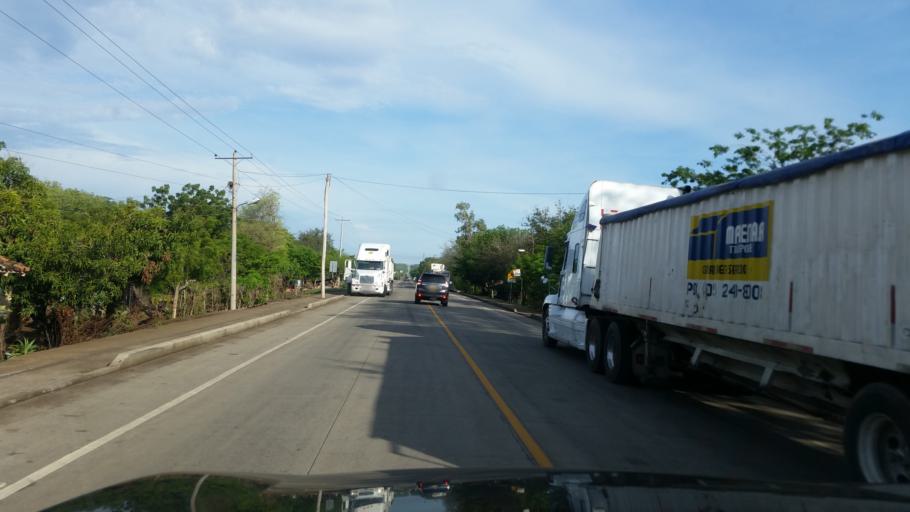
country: NI
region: Managua
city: Carlos Fonseca Amador
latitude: 12.1058
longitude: -86.5855
